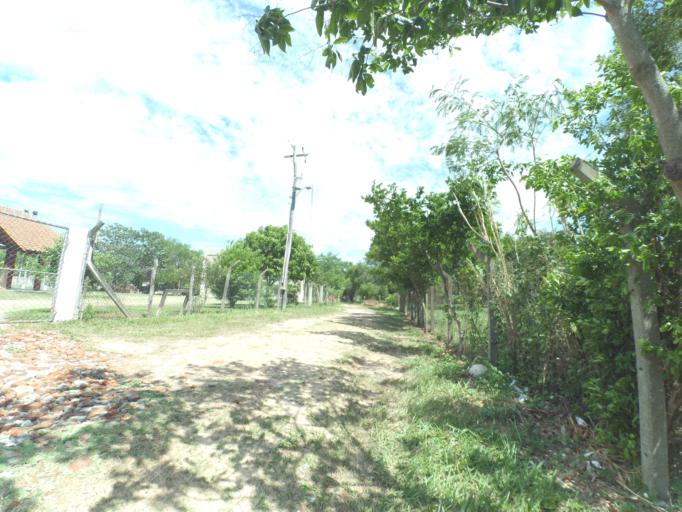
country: BO
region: Santa Cruz
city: Santa Cruz de la Sierra
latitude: -17.8120
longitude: -63.2352
